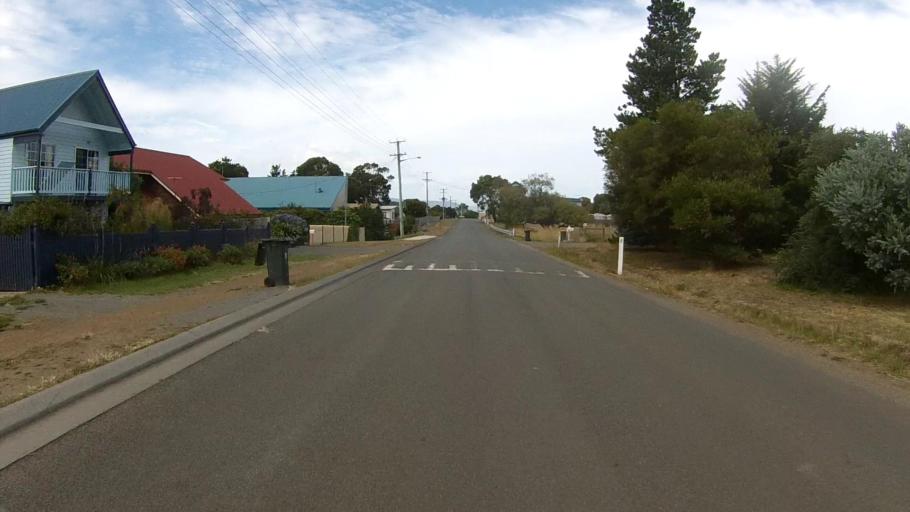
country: AU
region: Tasmania
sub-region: Clarence
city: Sandford
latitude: -42.9885
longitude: 147.5202
